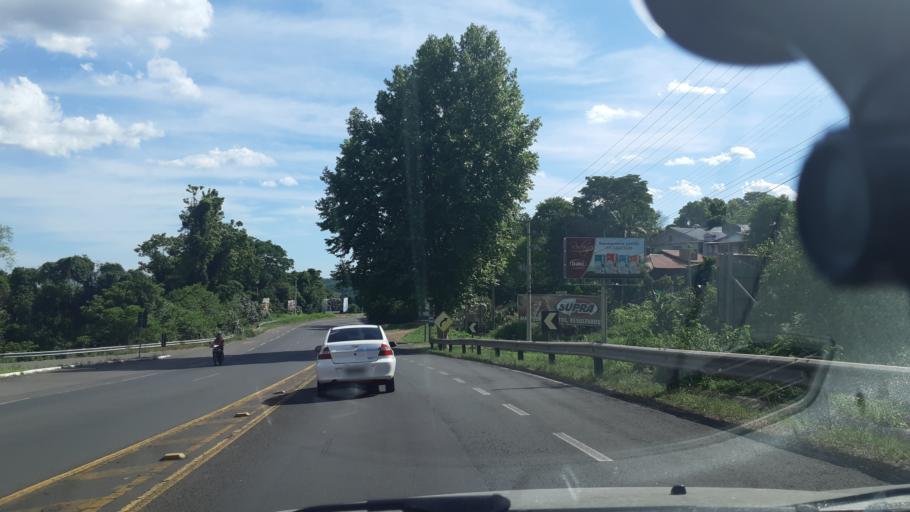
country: BR
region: Rio Grande do Sul
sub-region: Estancia Velha
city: Estancia Velha
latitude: -29.6266
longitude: -51.1380
